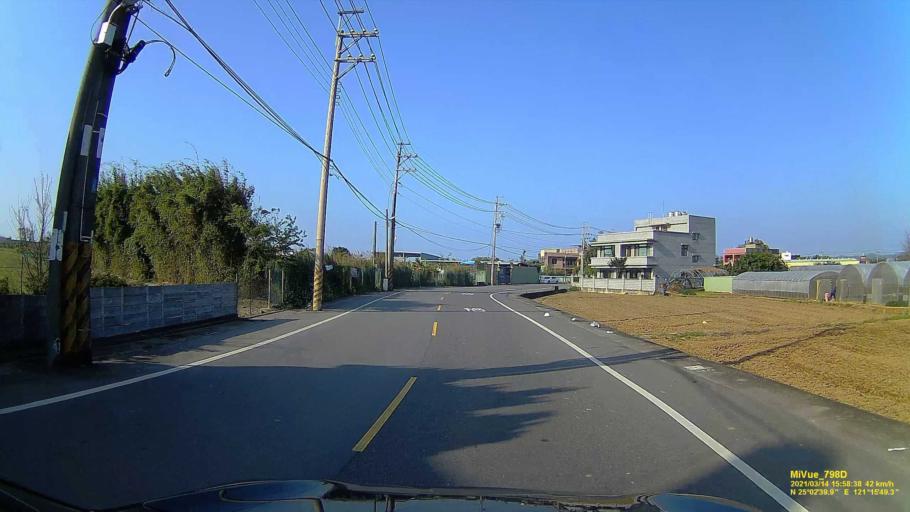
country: TW
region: Taiwan
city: Taoyuan City
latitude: 25.0445
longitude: 121.2636
